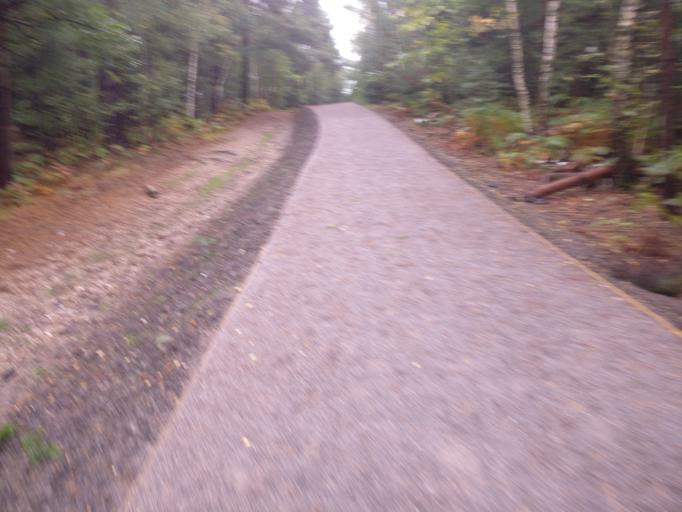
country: GB
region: England
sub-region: Surrey
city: Frimley
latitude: 51.3174
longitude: -0.7109
